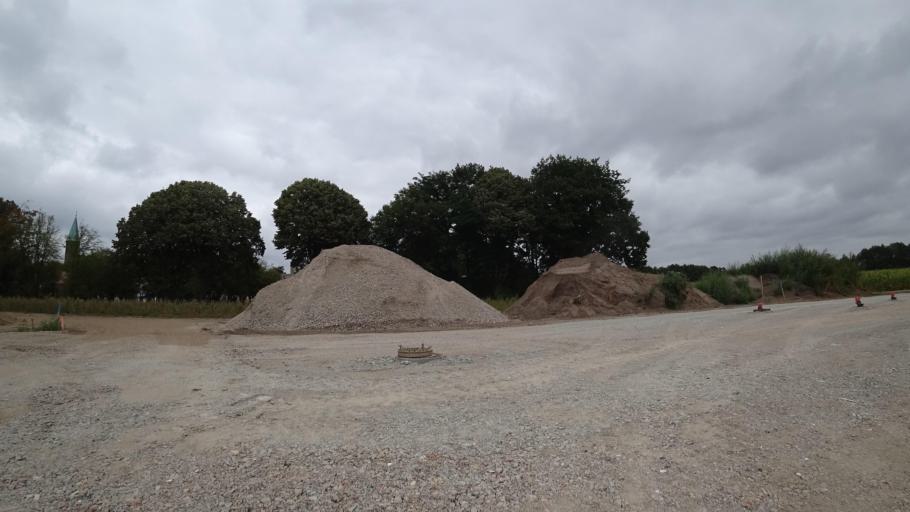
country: DE
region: North Rhine-Westphalia
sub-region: Regierungsbezirk Detmold
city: Guetersloh
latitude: 51.9114
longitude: 8.4354
